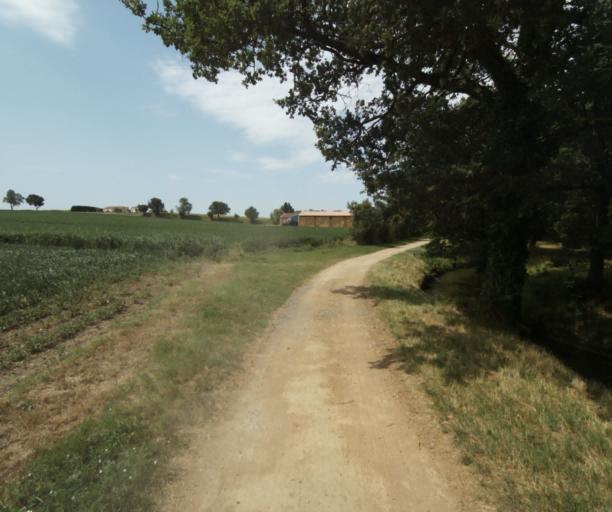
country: FR
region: Midi-Pyrenees
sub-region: Departement de la Haute-Garonne
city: Saint-Felix-Lauragais
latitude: 43.4291
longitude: 1.9122
